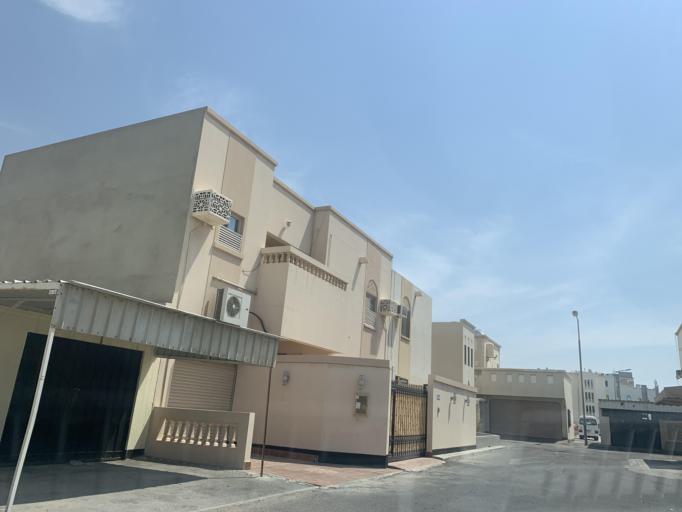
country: BH
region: Central Governorate
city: Madinat Hamad
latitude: 26.1346
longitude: 50.5001
